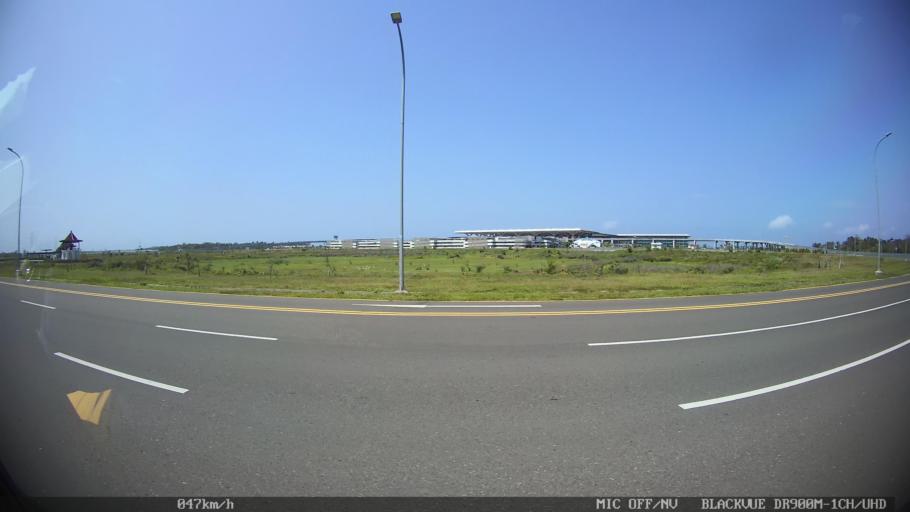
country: ID
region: Daerah Istimewa Yogyakarta
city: Srandakan
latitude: -7.8919
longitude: 110.0590
